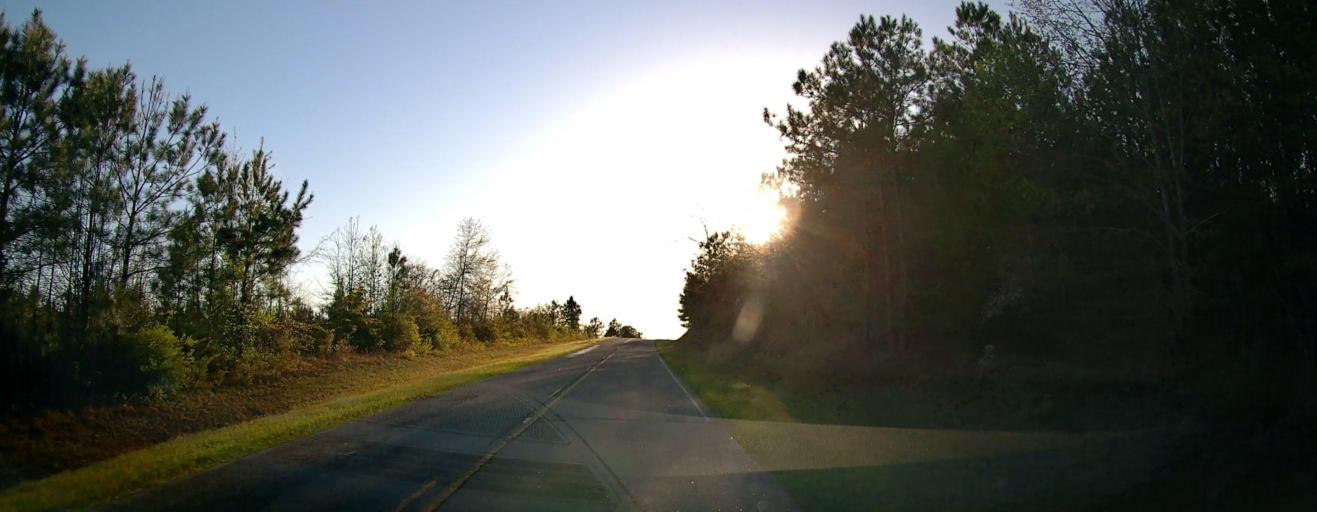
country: US
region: Georgia
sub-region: Wilkinson County
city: Gordon
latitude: 32.8781
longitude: -83.2651
